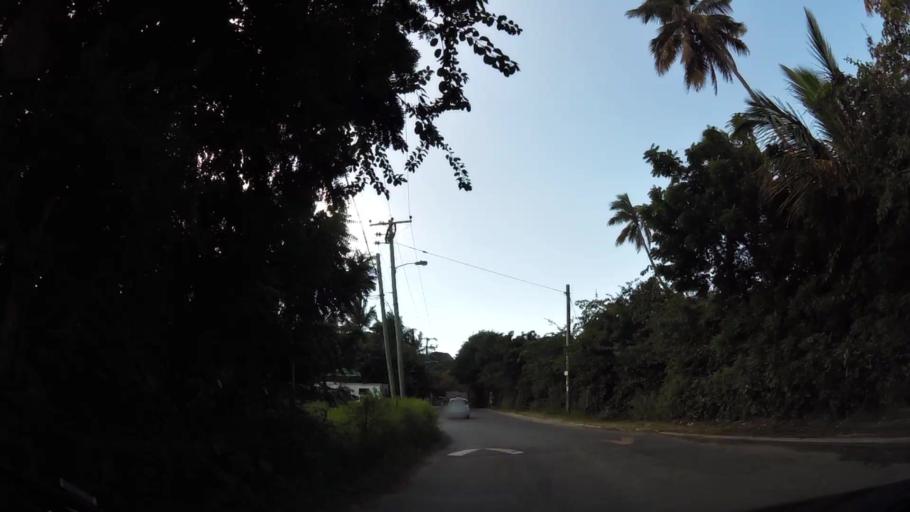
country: VG
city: Tortola
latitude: 18.4441
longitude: -64.4387
